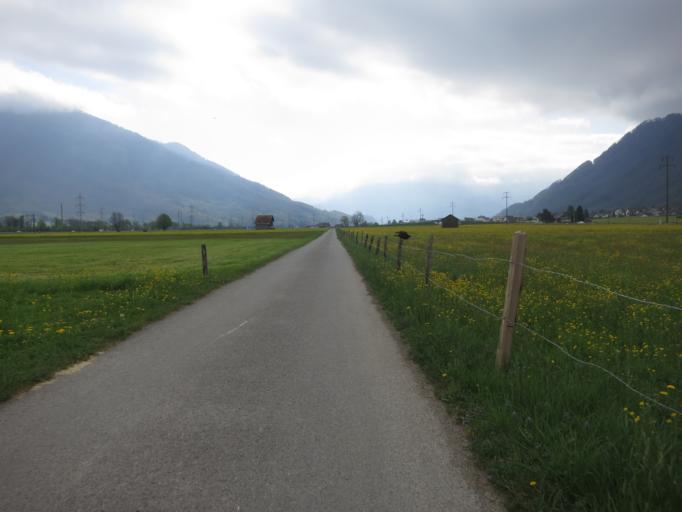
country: CH
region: Glarus
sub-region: Glarus
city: Bilten
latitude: 47.1619
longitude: 9.0131
